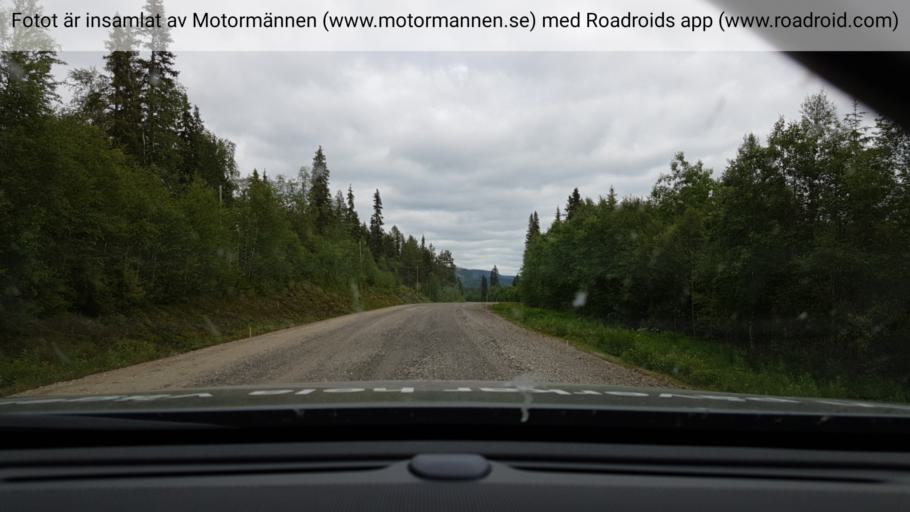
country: SE
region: Vaesterbotten
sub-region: Storumans Kommun
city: Fristad
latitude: 65.8167
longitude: 16.7802
